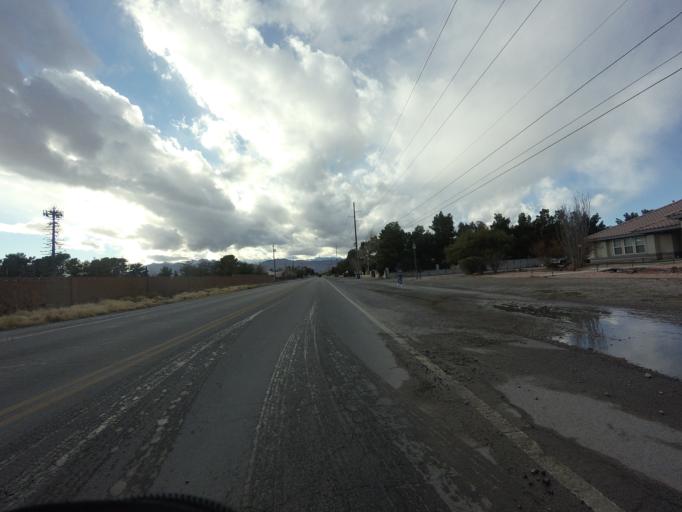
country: US
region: Nevada
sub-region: Clark County
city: Las Vegas
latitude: 36.2687
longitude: -115.2297
